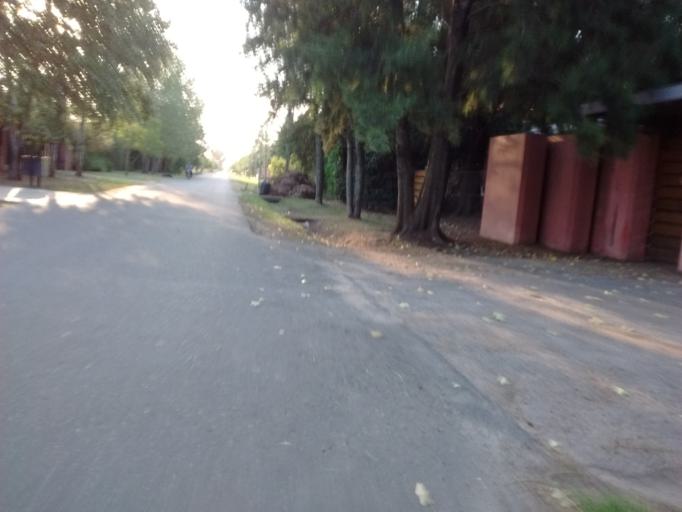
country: AR
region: Santa Fe
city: Funes
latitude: -32.9161
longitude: -60.7584
